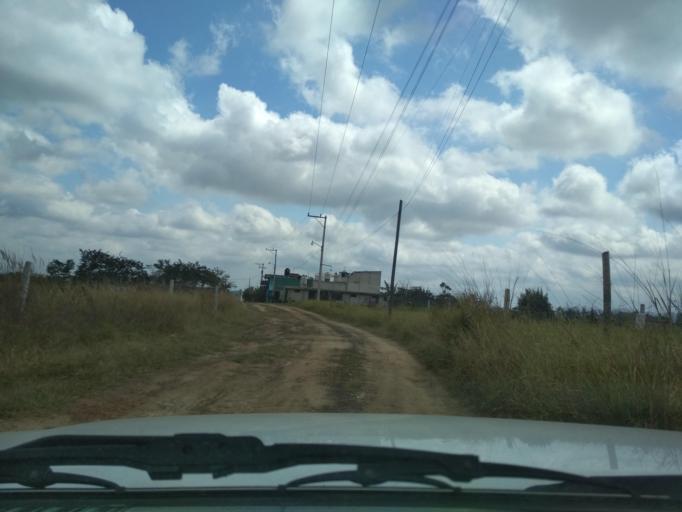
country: MX
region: Veracruz
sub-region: Emiliano Zapata
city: Jacarandas
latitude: 19.4967
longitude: -96.8407
